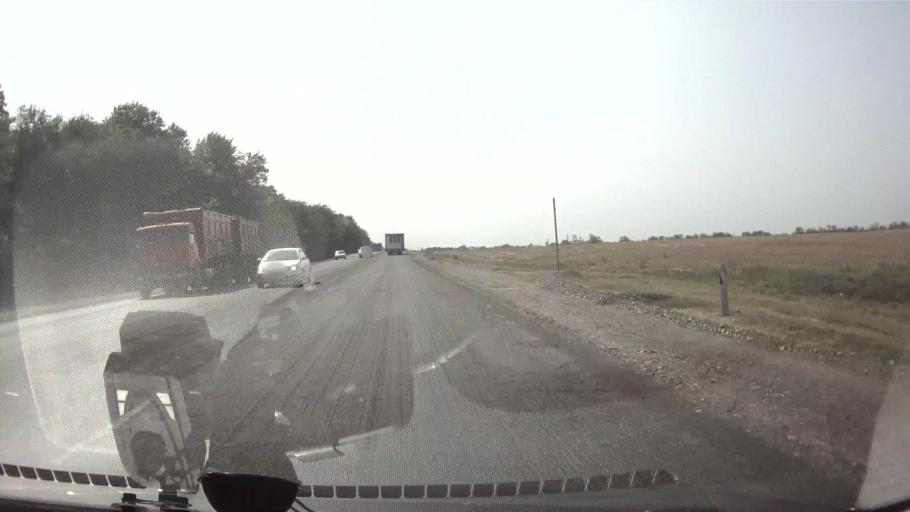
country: RU
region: Krasnodarskiy
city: Ladozhskaya
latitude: 45.3274
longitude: 39.9335
